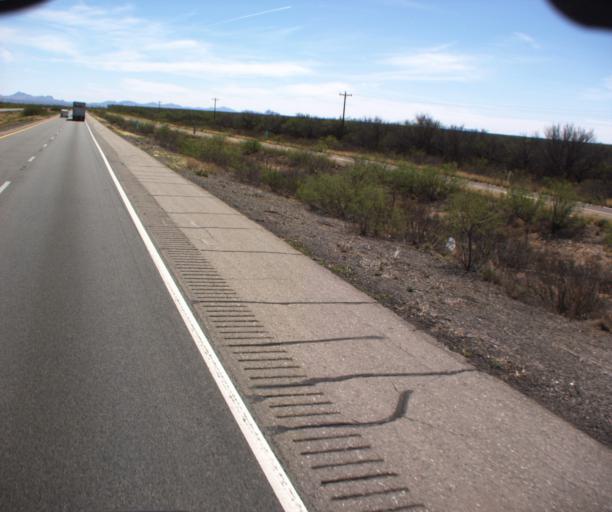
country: US
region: Arizona
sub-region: Cochise County
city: Willcox
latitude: 32.2958
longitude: -109.3482
